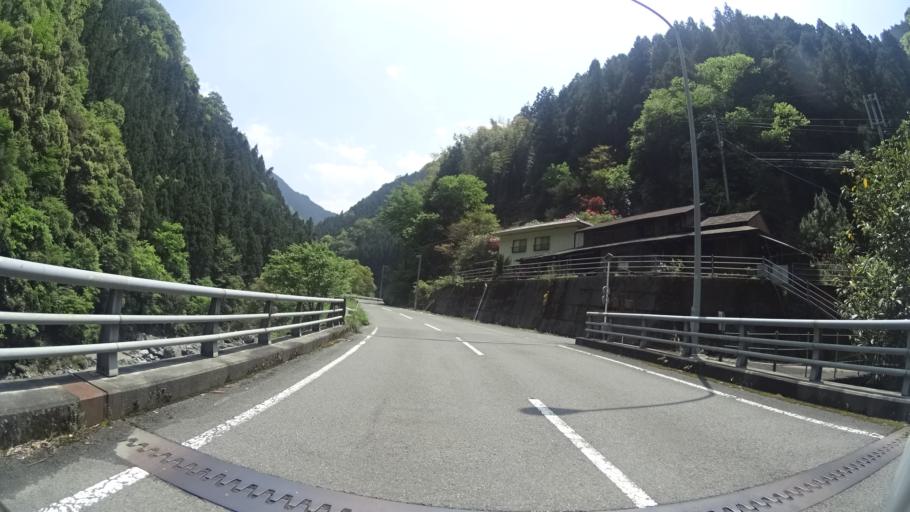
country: JP
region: Tokushima
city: Wakimachi
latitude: 33.9737
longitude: 134.0801
